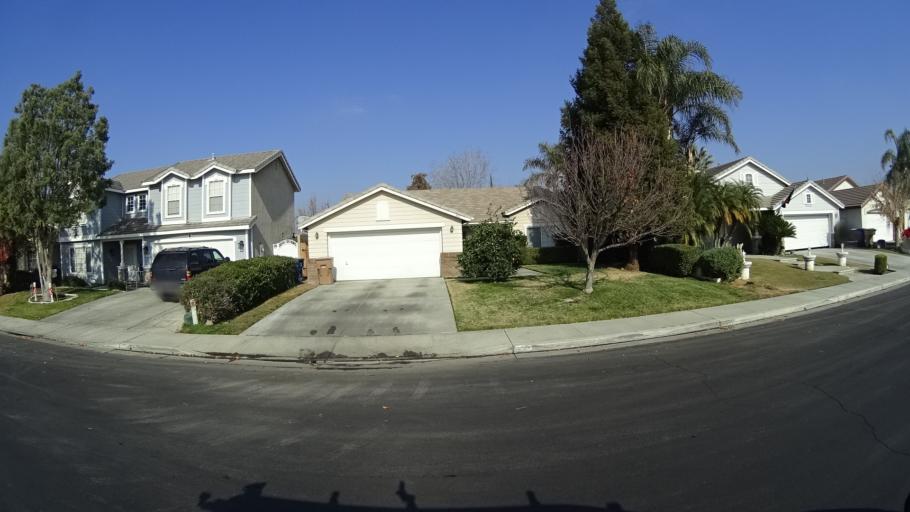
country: US
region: California
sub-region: Kern County
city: Greenacres
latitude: 35.3080
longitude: -119.0823
